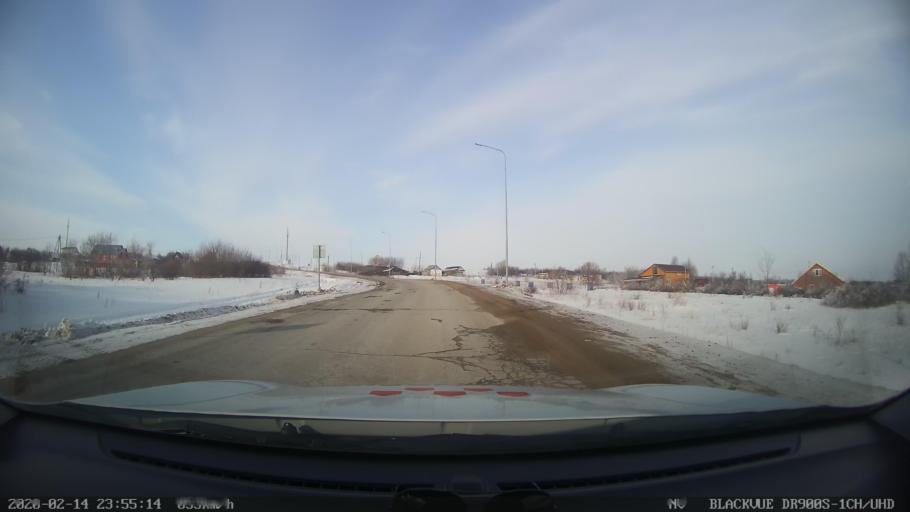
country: RU
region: Tatarstan
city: Kuybyshevskiy Zaton
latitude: 55.3152
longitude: 49.1444
